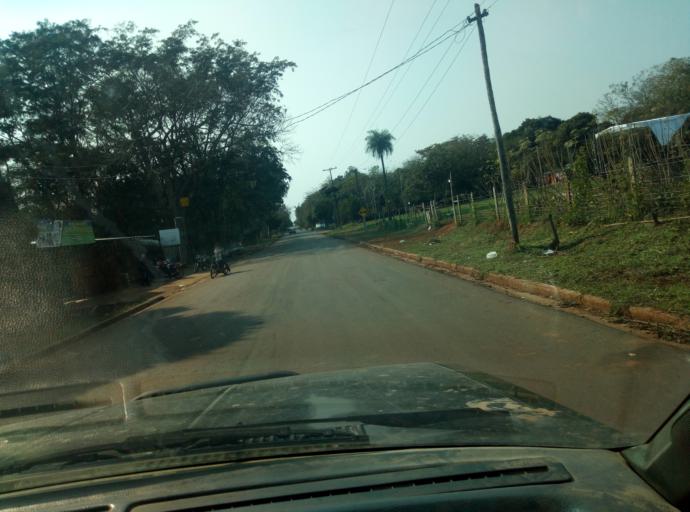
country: PY
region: Caaguazu
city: Carayao
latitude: -25.2105
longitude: -56.2993
